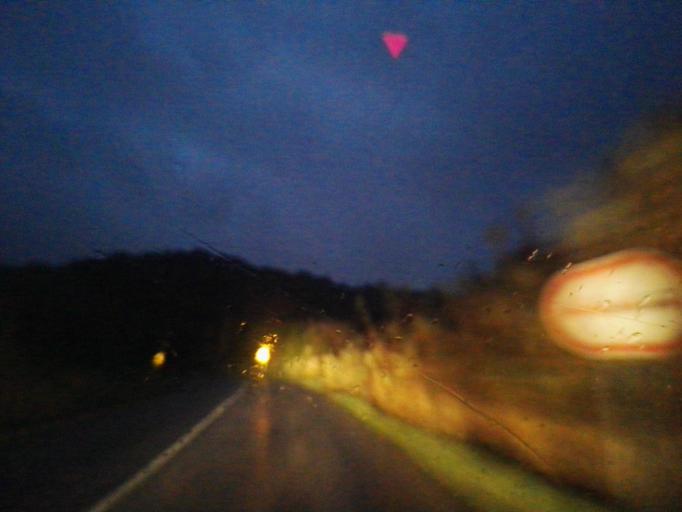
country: PT
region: Santarem
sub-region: Cartaxo
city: Cartaxo
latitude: 39.2650
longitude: -8.8109
